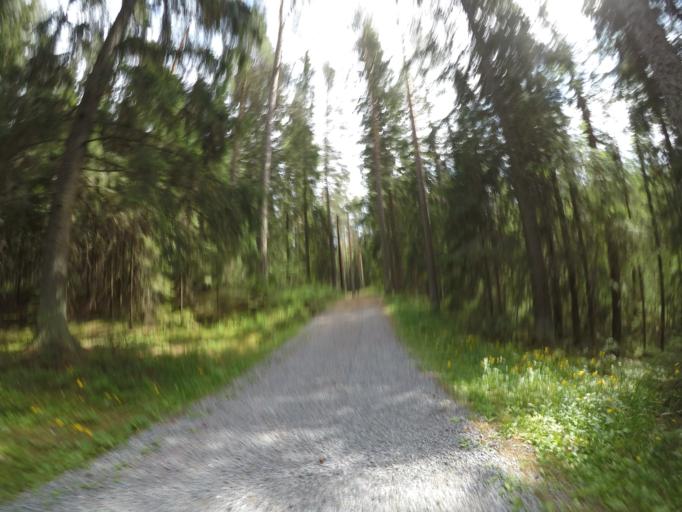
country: FI
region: Haeme
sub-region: Haemeenlinna
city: Haemeenlinna
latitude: 60.9979
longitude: 24.4065
